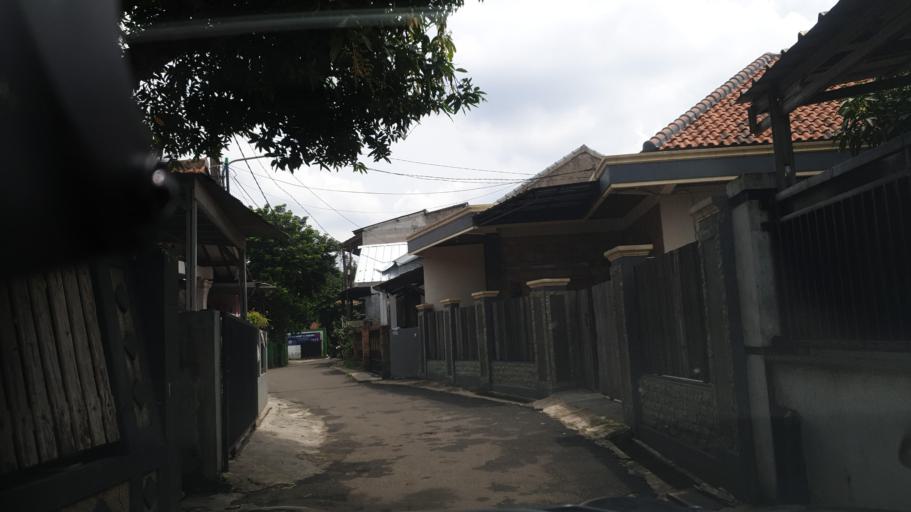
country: ID
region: West Java
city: Pamulang
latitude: -6.3379
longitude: 106.7688
